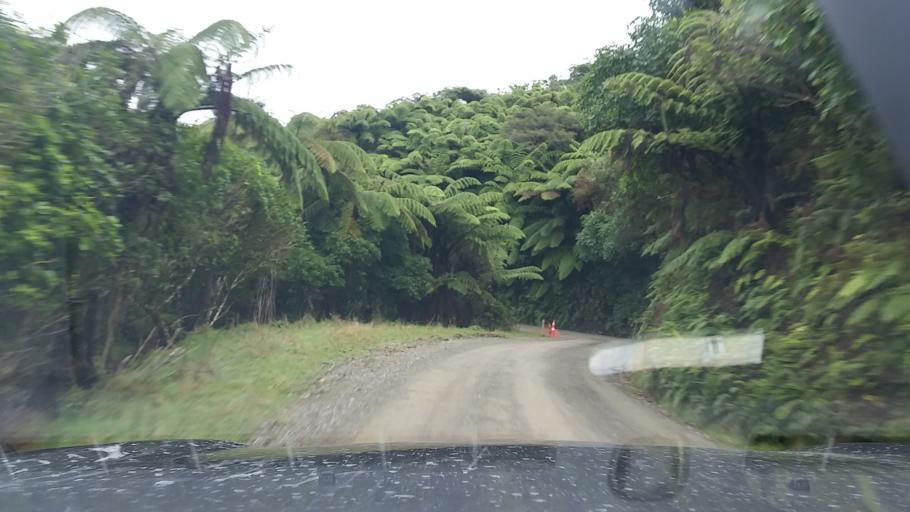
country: NZ
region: Marlborough
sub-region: Marlborough District
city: Picton
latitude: -41.1787
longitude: 173.9898
